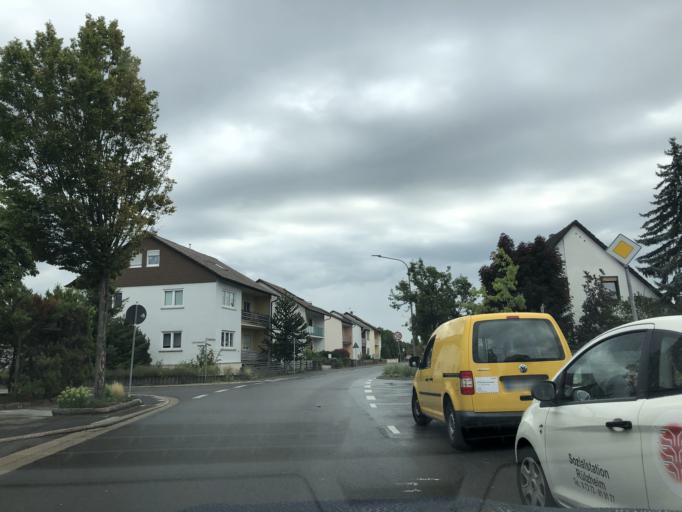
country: DE
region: Rheinland-Pfalz
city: Bellheim
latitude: 49.1971
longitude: 8.2910
